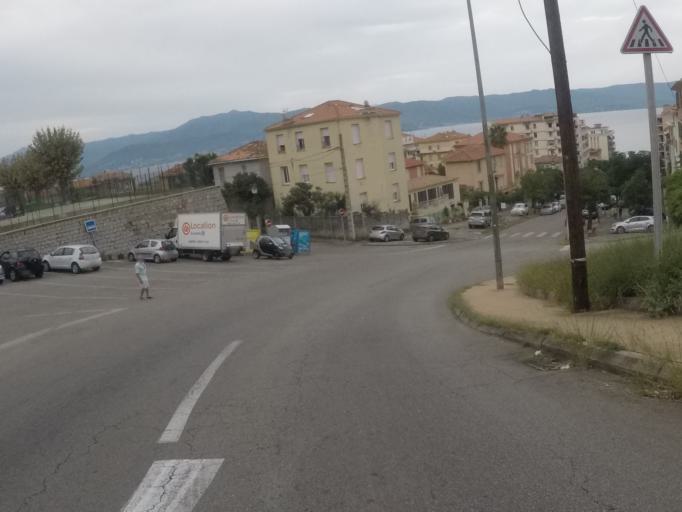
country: FR
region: Corsica
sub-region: Departement de la Corse-du-Sud
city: Ajaccio
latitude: 41.9159
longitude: 8.7237
